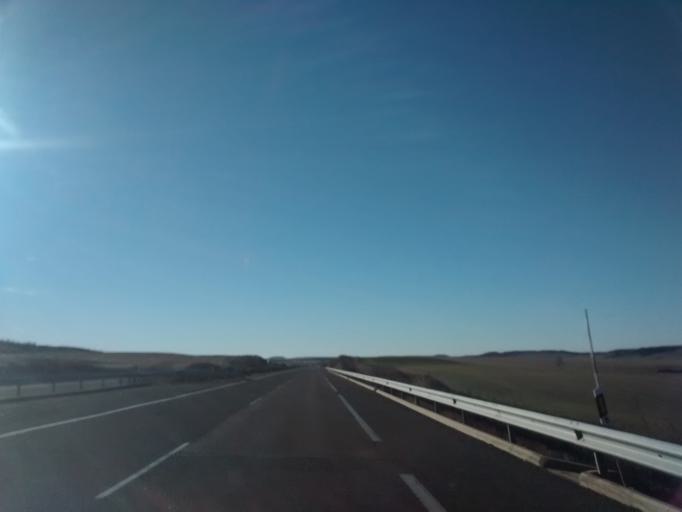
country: ES
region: Castille and Leon
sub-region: Provincia de Palencia
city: Pradanos de Ojeda
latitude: 42.6443
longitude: -4.3513
